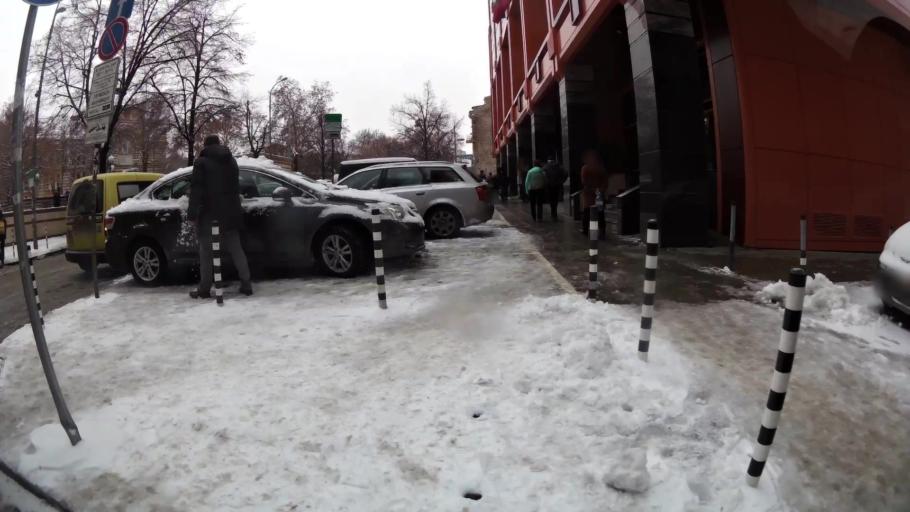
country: BG
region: Sofia-Capital
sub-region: Stolichna Obshtina
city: Sofia
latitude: 42.7003
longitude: 23.3243
